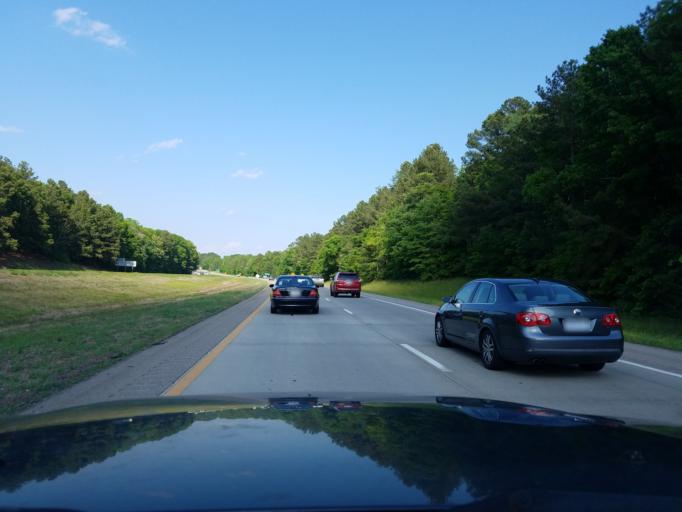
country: US
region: North Carolina
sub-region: Vance County
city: South Henderson
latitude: 36.3194
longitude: -78.4692
